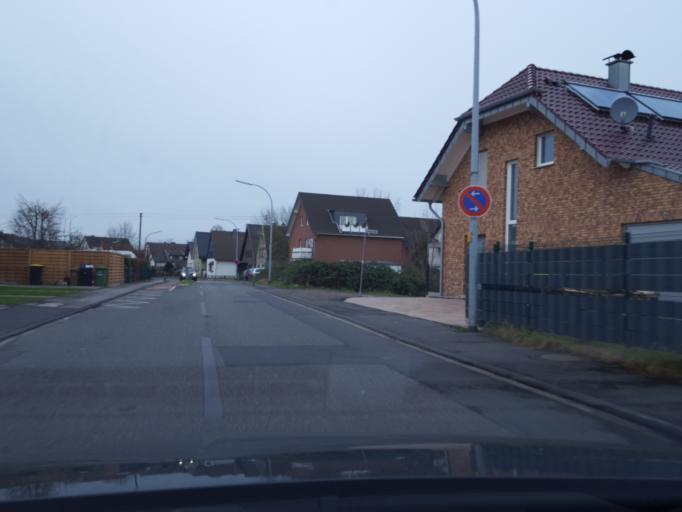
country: DE
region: North Rhine-Westphalia
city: Niederkassel
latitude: 50.7815
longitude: 7.0549
